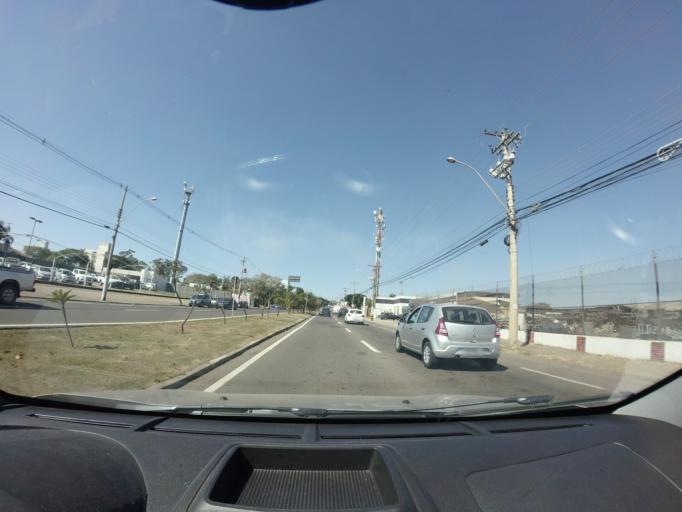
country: BR
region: Sao Paulo
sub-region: Piracicaba
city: Piracicaba
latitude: -22.7288
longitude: -47.6175
